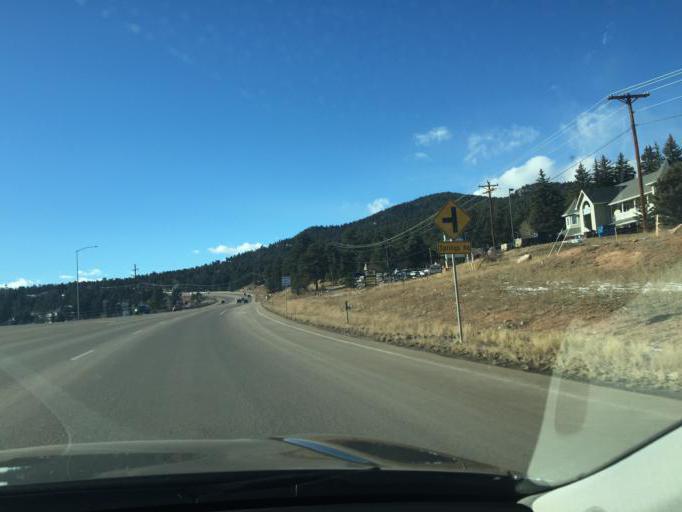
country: US
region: Colorado
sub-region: Jefferson County
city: Evergreen
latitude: 39.5019
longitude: -105.3233
